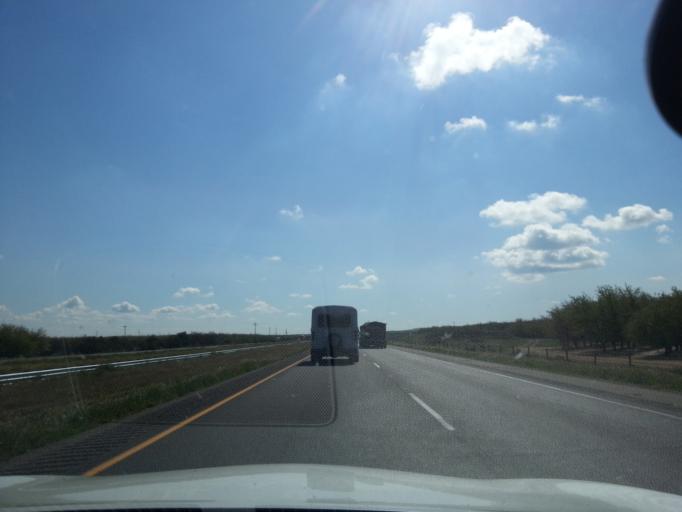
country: US
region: California
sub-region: Fresno County
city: Coalinga
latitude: 36.3957
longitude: -120.3586
